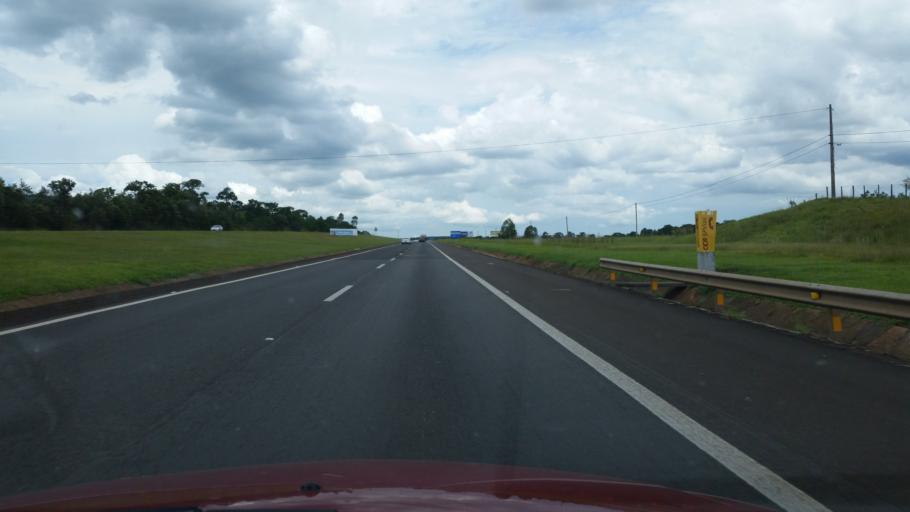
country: BR
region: Sao Paulo
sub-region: Itatinga
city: Itatinga
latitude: -23.1522
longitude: -48.3884
